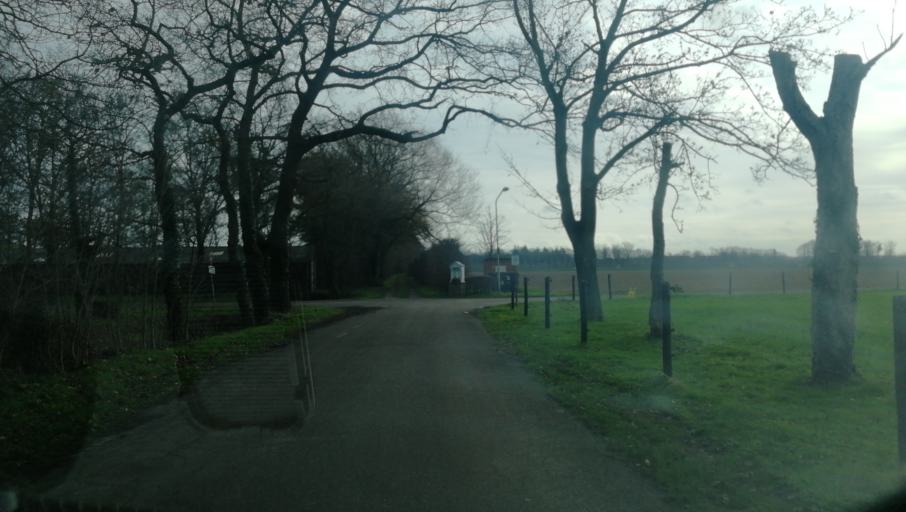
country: NL
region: Limburg
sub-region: Gemeente Beesel
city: Offenbeek
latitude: 51.2996
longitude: 6.1034
